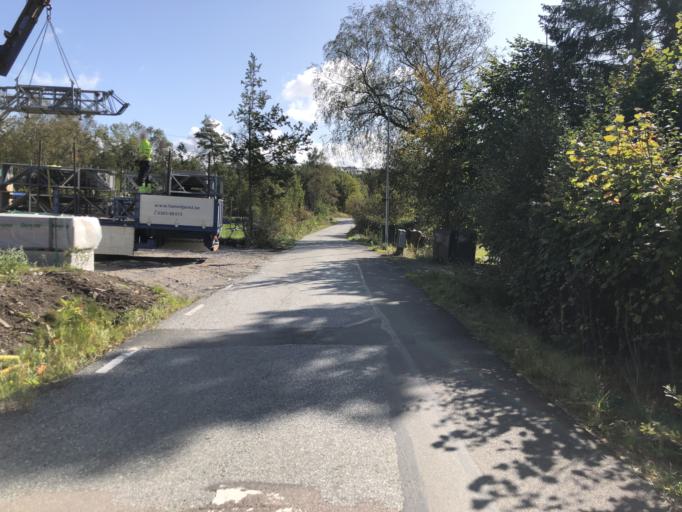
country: SE
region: Vaestra Goetaland
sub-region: Goteborg
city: Torslanda
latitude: 57.7367
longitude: 11.8370
